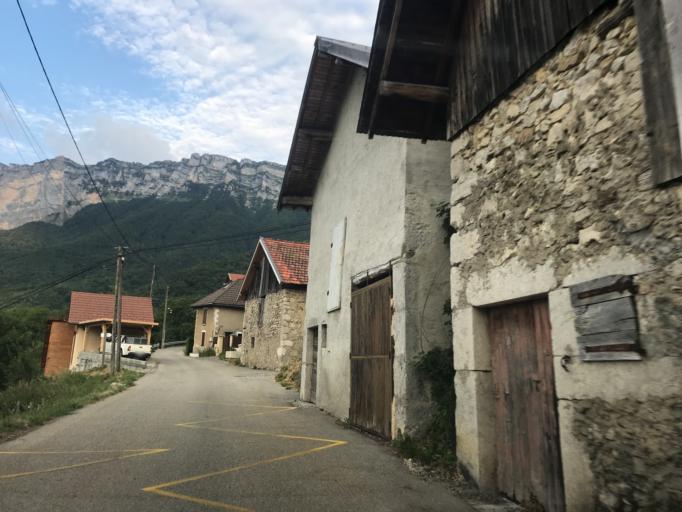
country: FR
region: Rhone-Alpes
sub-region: Departement de l'Isere
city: Saint-Vincent-de-Mercuze
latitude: 45.3951
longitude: 5.9444
